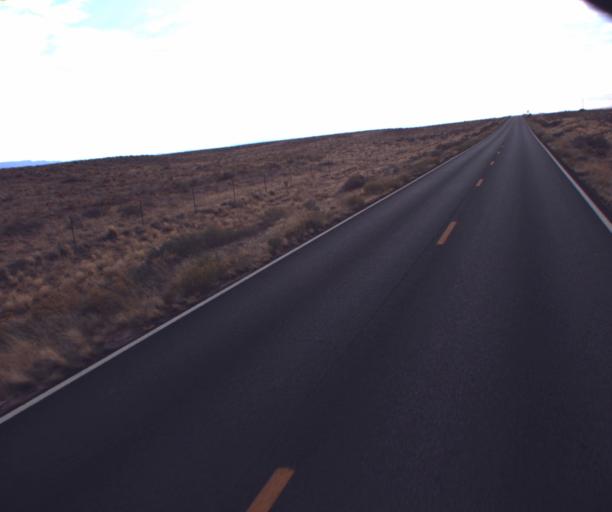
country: US
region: Arizona
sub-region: Apache County
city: Many Farms
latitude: 36.5558
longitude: -109.5355
